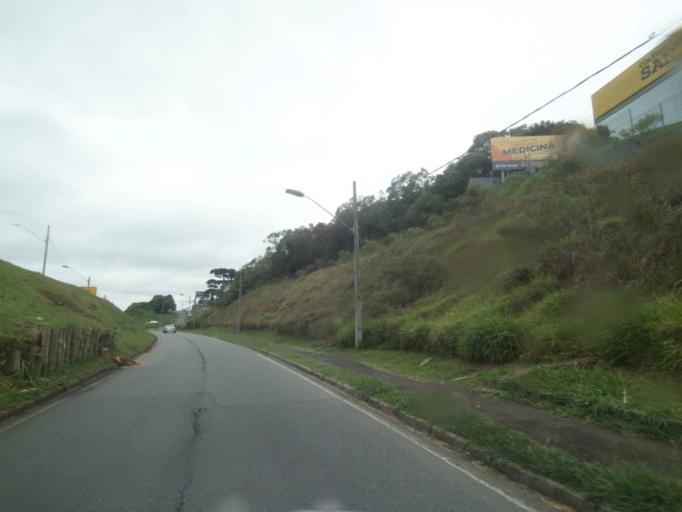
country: BR
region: Parana
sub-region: Curitiba
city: Curitiba
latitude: -25.4313
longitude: -49.3242
